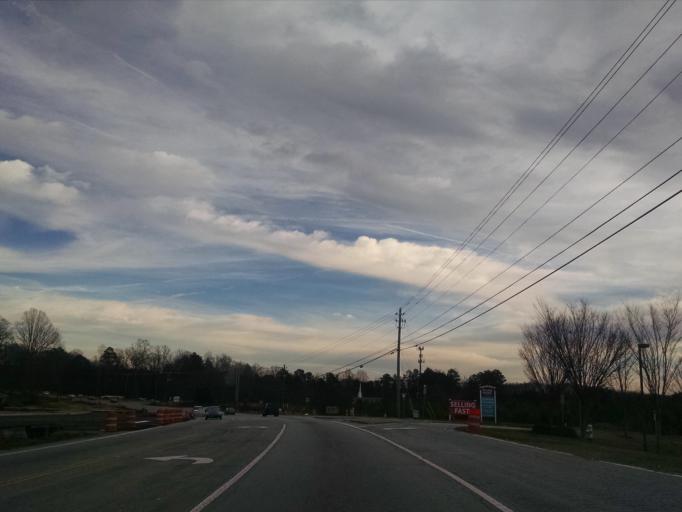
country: US
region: Georgia
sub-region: Gwinnett County
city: Sugar Hill
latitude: 34.1131
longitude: -84.0731
